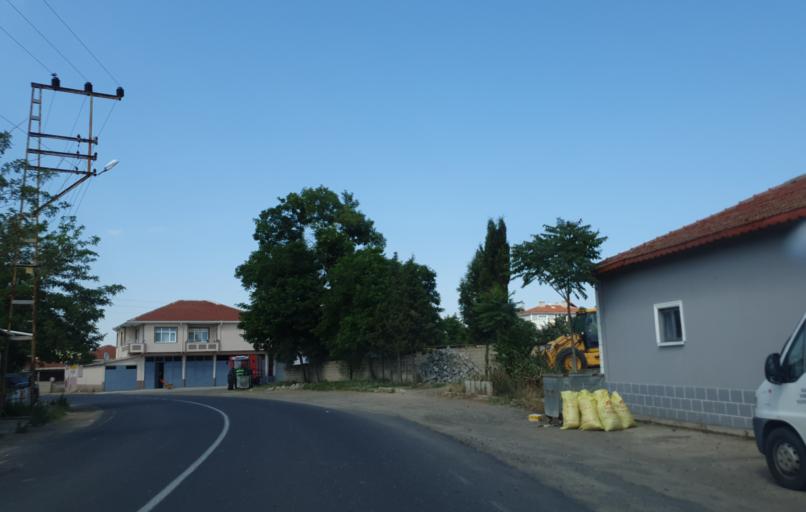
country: TR
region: Tekirdag
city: Muratli
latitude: 41.2190
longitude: 27.5440
